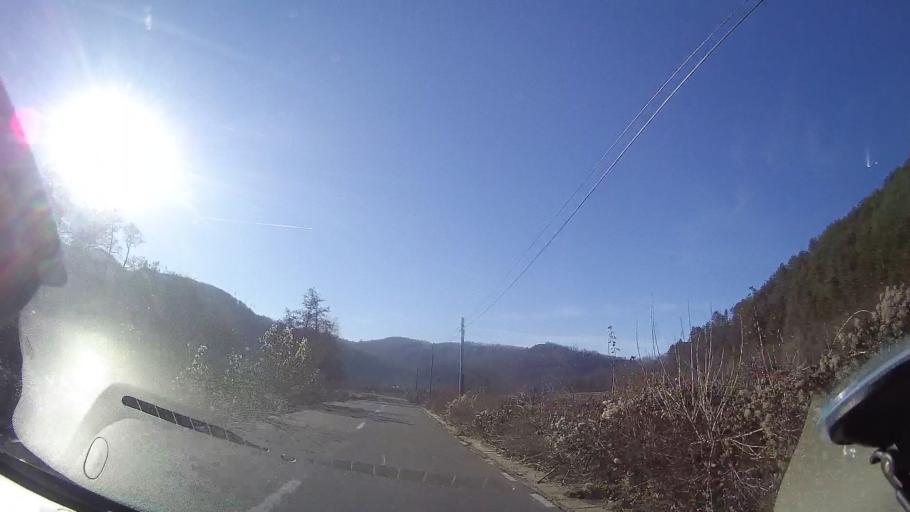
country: RO
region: Bihor
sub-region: Comuna Bratca
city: Bratca
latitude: 46.9239
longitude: 22.6269
